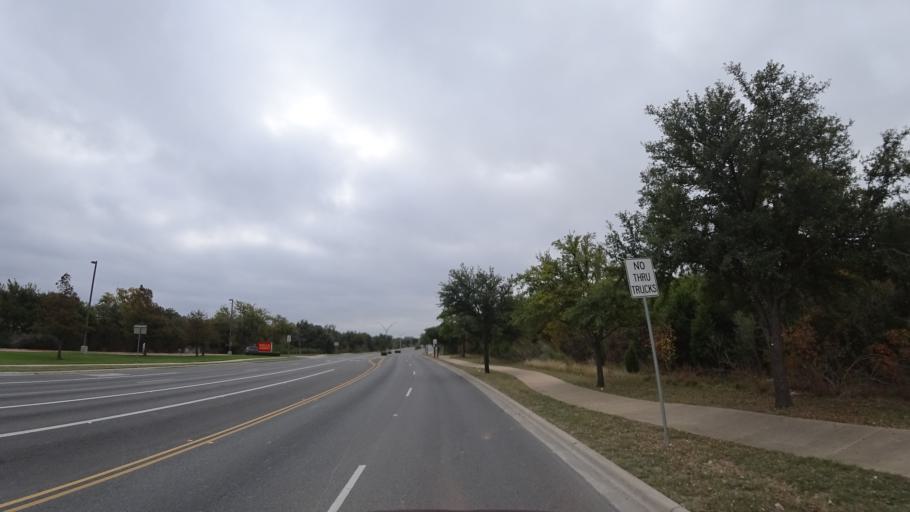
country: US
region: Texas
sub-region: Williamson County
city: Cedar Park
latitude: 30.5141
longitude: -97.8510
